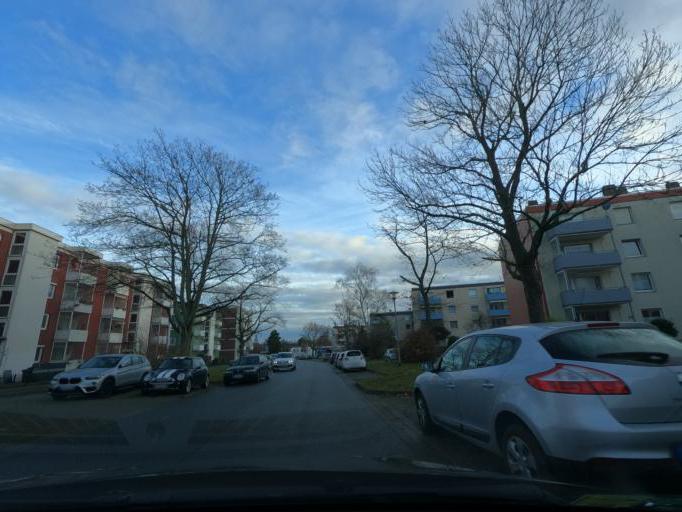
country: DE
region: Lower Saxony
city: Wolfenbuettel
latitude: 52.1585
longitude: 10.5236
